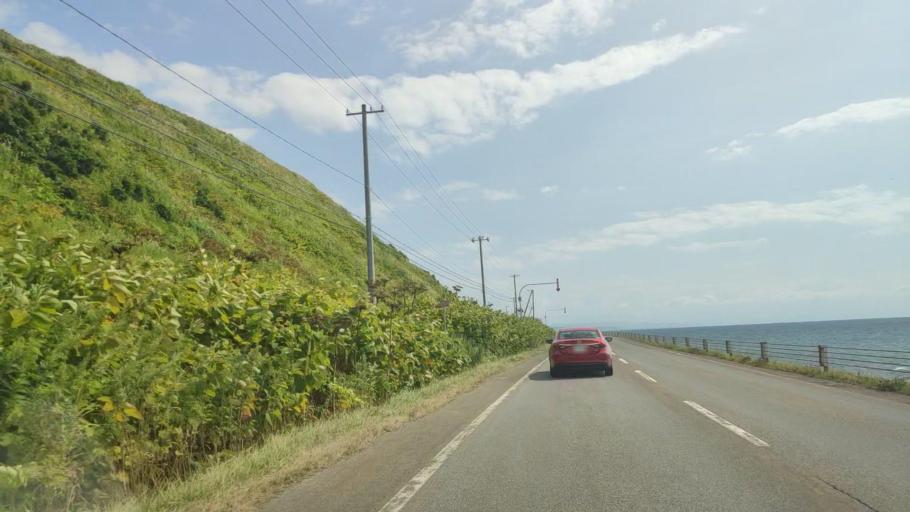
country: JP
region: Hokkaido
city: Rumoi
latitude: 44.0926
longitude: 141.6610
